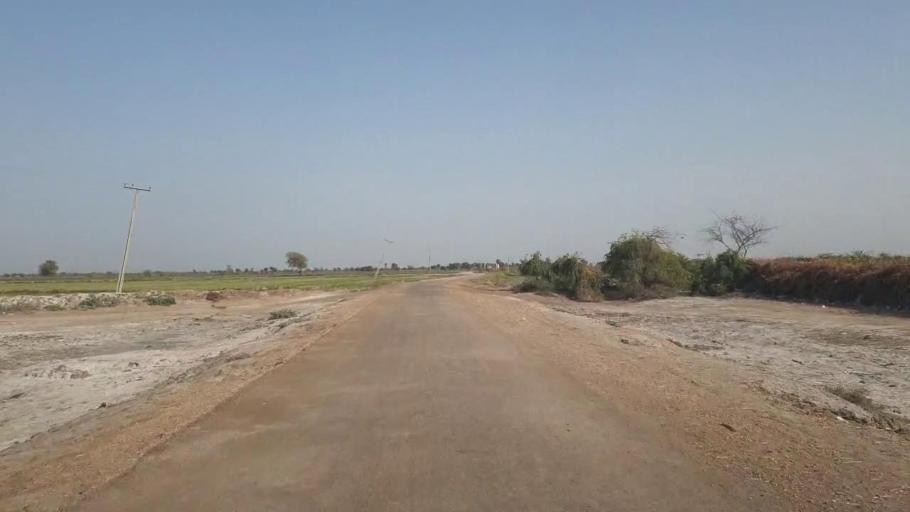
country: PK
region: Sindh
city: Dhoro Naro
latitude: 25.4636
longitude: 69.5552
